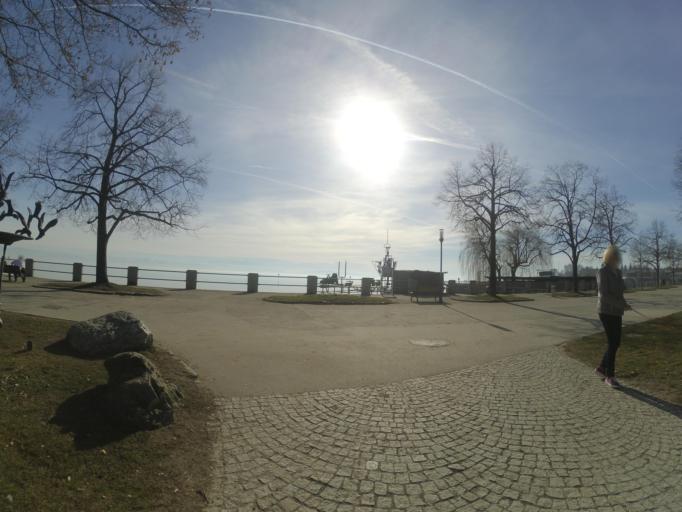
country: DE
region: Baden-Wuerttemberg
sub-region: Tuebingen Region
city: Friedrichshafen
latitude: 47.6513
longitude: 9.4747
